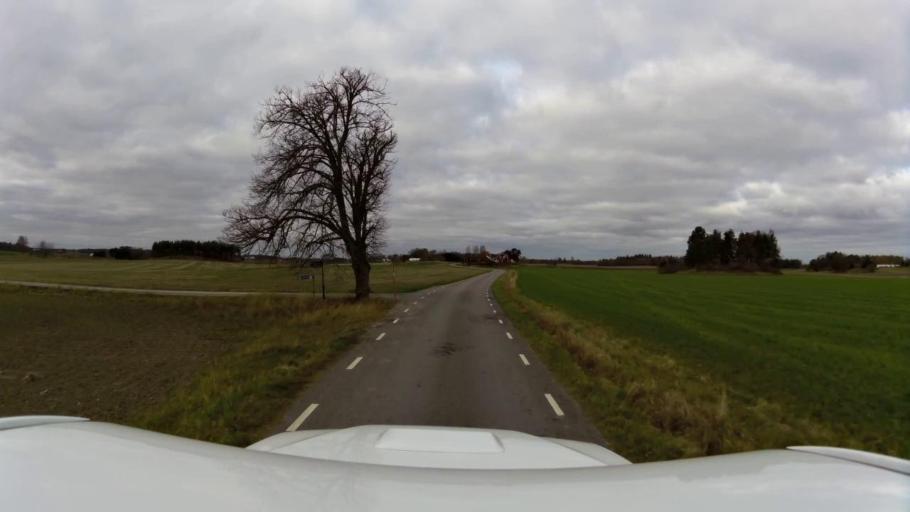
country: SE
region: OEstergoetland
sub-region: Linkopings Kommun
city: Linghem
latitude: 58.3956
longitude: 15.7935
